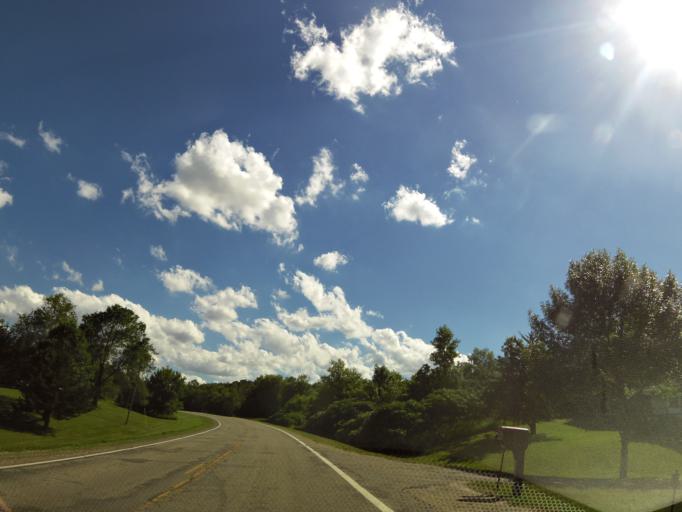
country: US
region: Minnesota
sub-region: Meeker County
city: Dassel
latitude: 45.1022
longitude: -94.3062
